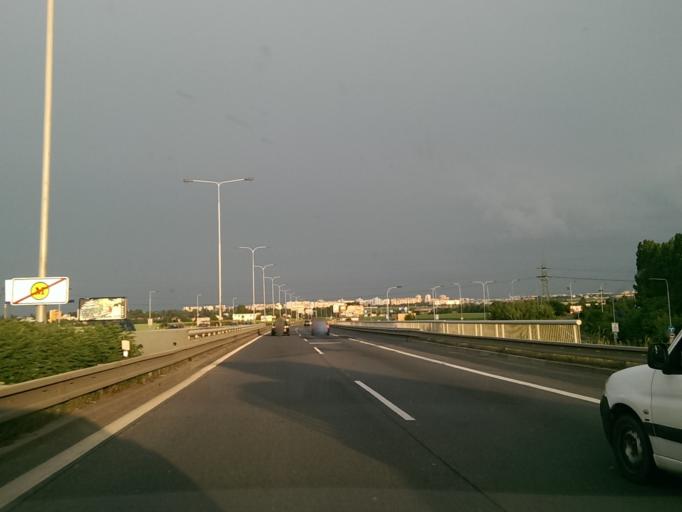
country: CZ
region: Praha
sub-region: Praha 9
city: Strizkov
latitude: 50.1575
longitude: 14.4845
